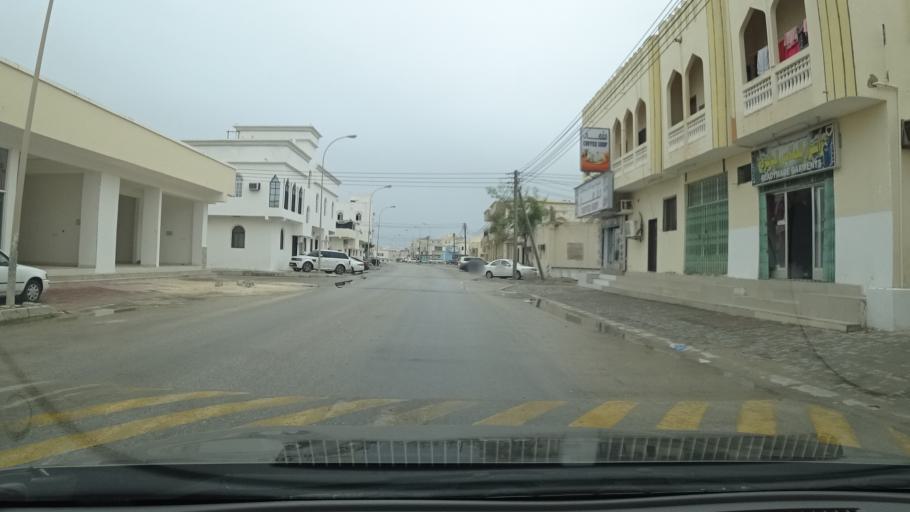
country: OM
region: Zufar
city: Salalah
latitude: 17.0235
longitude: 54.1589
